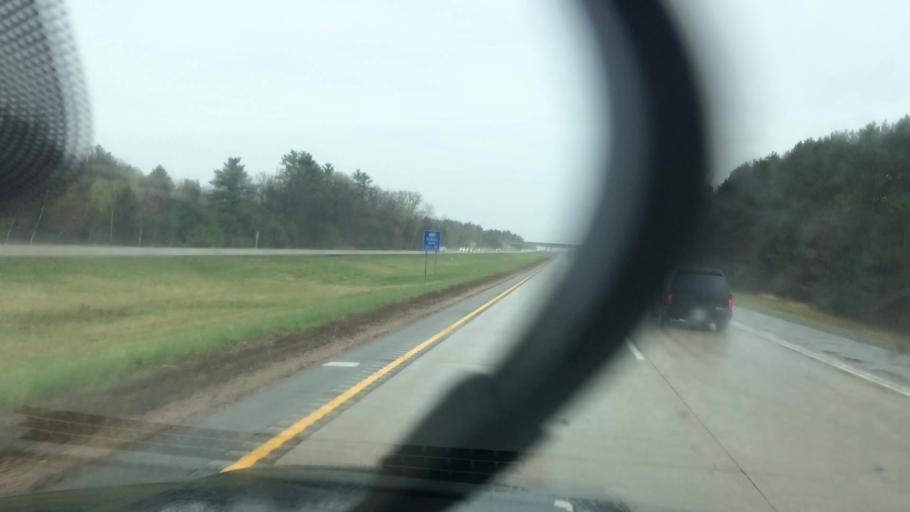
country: US
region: Wisconsin
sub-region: Portage County
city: Stevens Point
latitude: 44.6048
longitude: -89.6195
